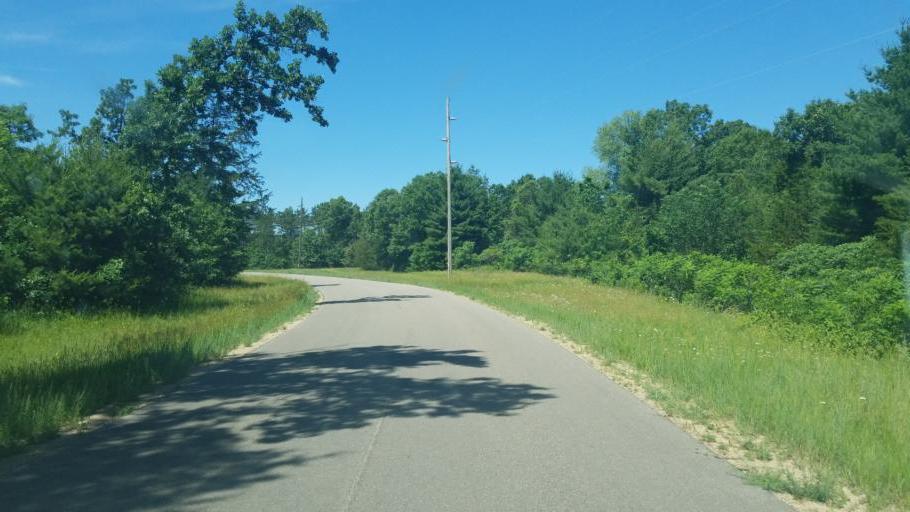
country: US
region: Wisconsin
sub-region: Juneau County
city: Mauston
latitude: 43.8694
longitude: -89.9462
